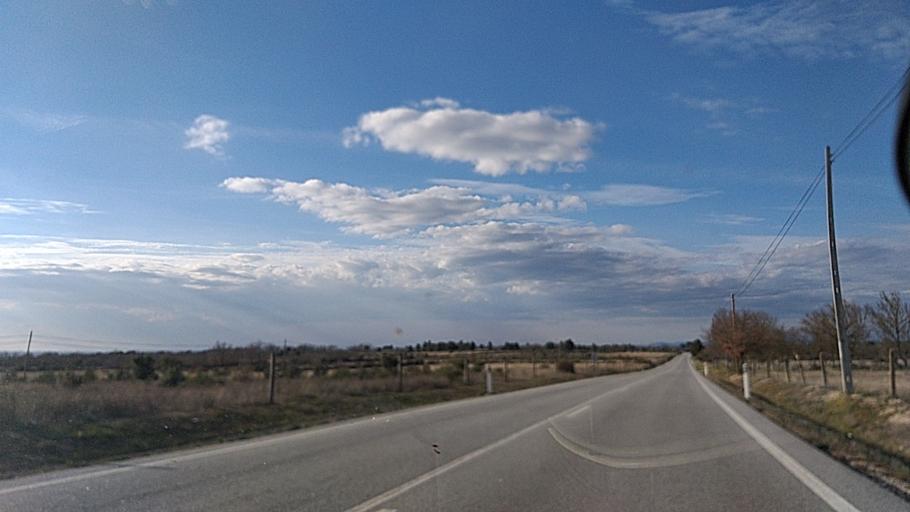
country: ES
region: Castille and Leon
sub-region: Provincia de Salamanca
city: Fuentes de Onoro
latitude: 40.6260
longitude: -6.8489
